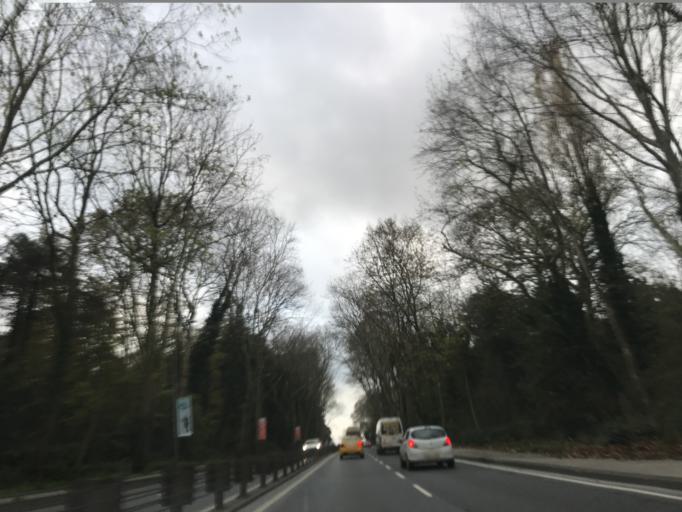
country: TR
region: Istanbul
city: Arikoey
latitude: 41.1455
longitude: 29.0280
